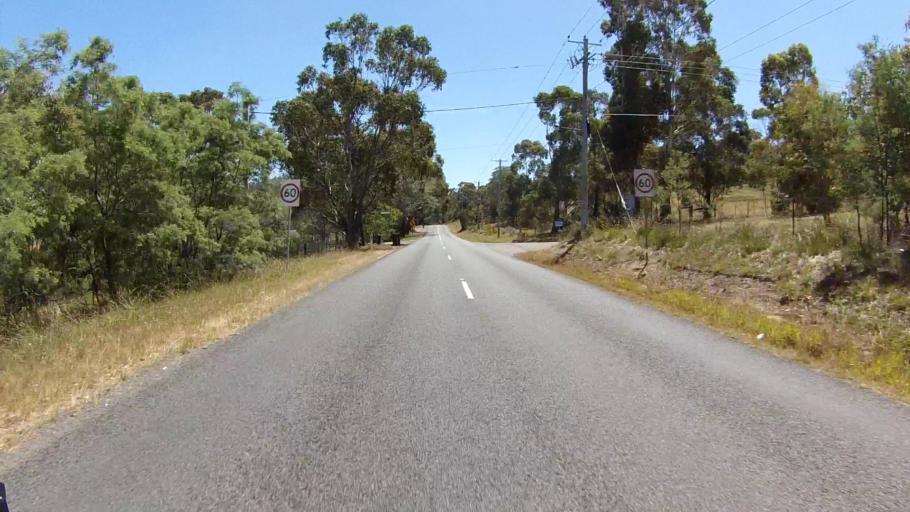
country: AU
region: Tasmania
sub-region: Clarence
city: Howrah
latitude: -42.8676
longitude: 147.4244
